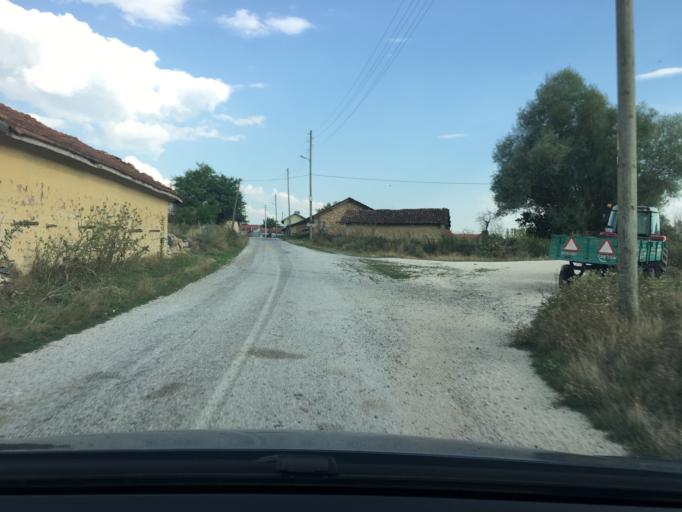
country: TR
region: Eskisehir
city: Kirka
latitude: 39.2790
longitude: 30.6747
